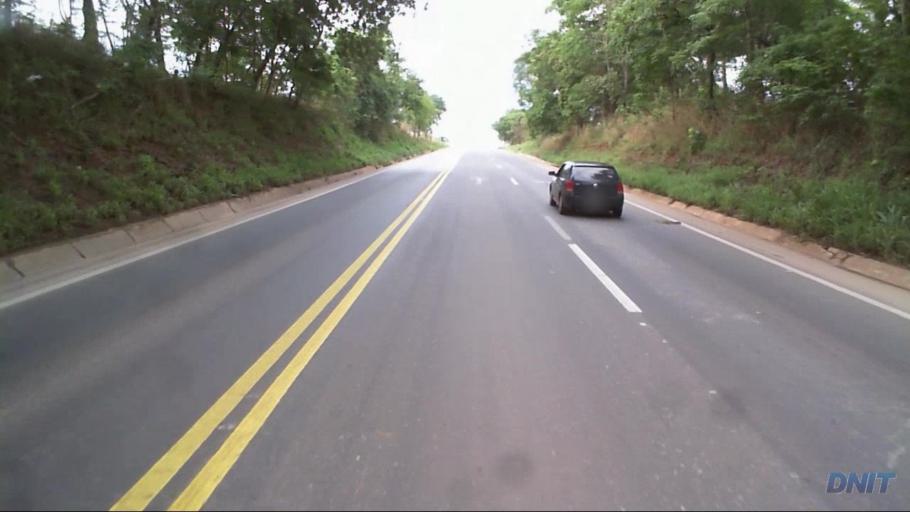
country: BR
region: Goias
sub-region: Uruacu
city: Uruacu
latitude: -14.6052
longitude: -49.1665
